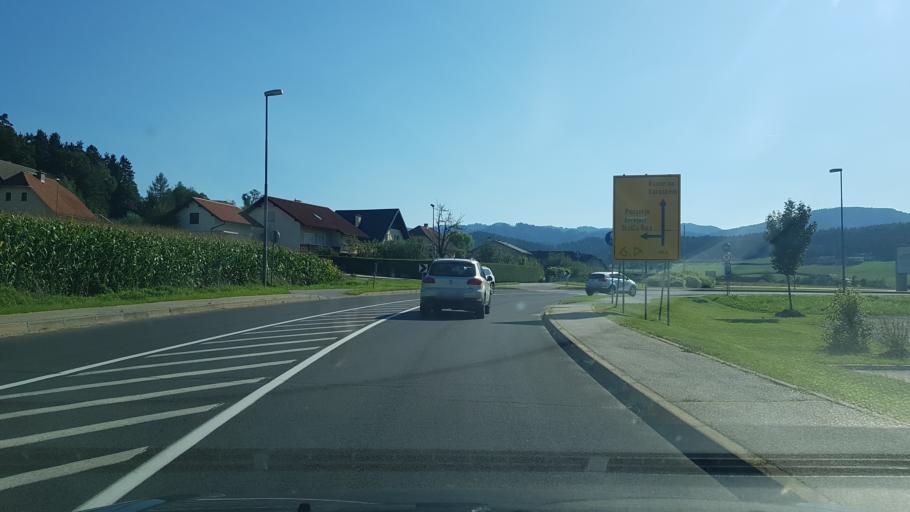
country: SI
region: Slovenj Gradec
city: Slovenj Gradec
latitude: 46.5007
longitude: 15.0738
